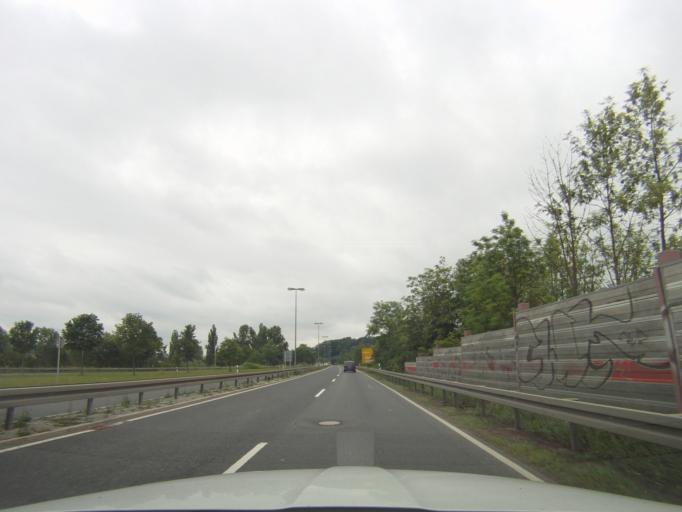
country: DE
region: Bavaria
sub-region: Upper Franconia
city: Coburg
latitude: 50.2733
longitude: 10.9555
